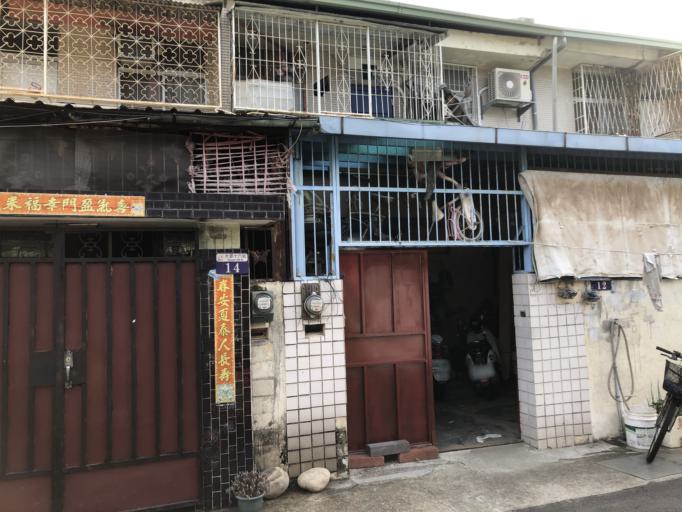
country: TW
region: Taiwan
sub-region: Taichung City
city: Taichung
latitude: 24.1425
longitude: 120.7235
